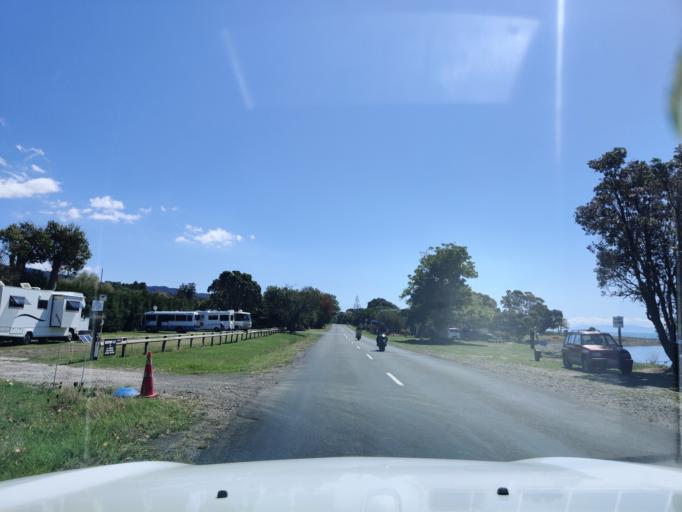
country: NZ
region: Waikato
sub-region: Thames-Coromandel District
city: Thames
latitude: -37.0500
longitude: 175.3002
